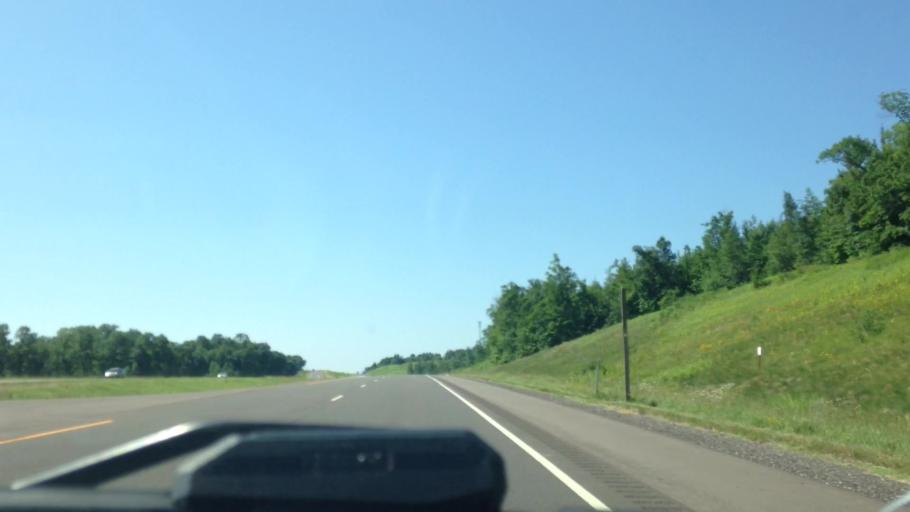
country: US
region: Wisconsin
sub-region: Washburn County
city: Spooner
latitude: 45.9712
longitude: -91.8277
